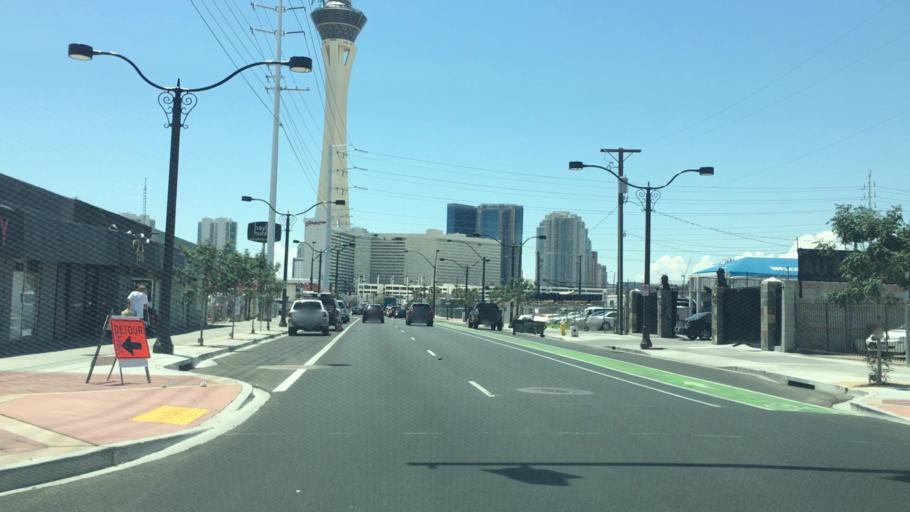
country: US
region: Nevada
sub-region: Clark County
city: Las Vegas
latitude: 36.1548
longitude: -115.1552
